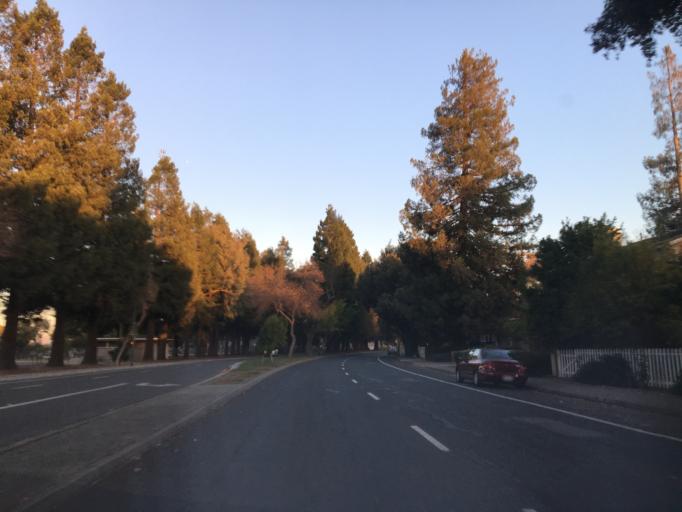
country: US
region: California
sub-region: Santa Clara County
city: Mountain View
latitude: 37.4096
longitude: -122.0868
